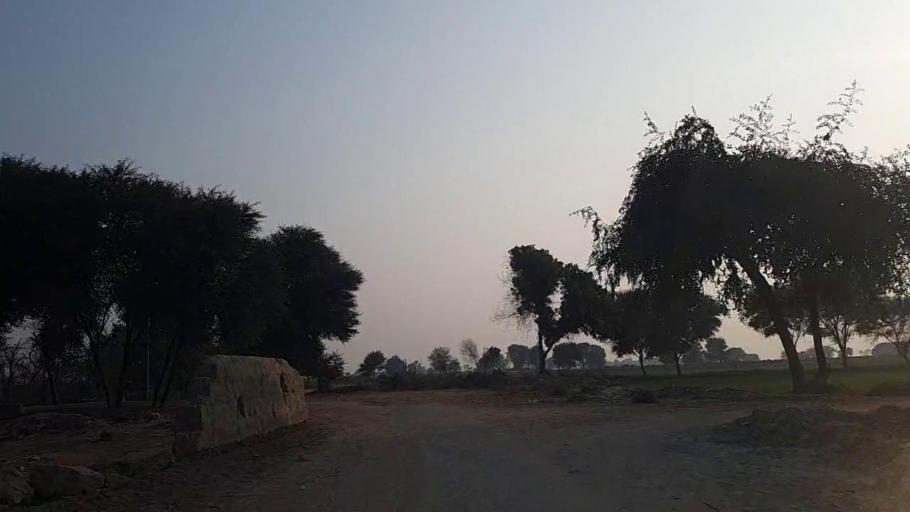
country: PK
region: Sindh
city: Nawabshah
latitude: 26.2094
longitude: 68.4710
